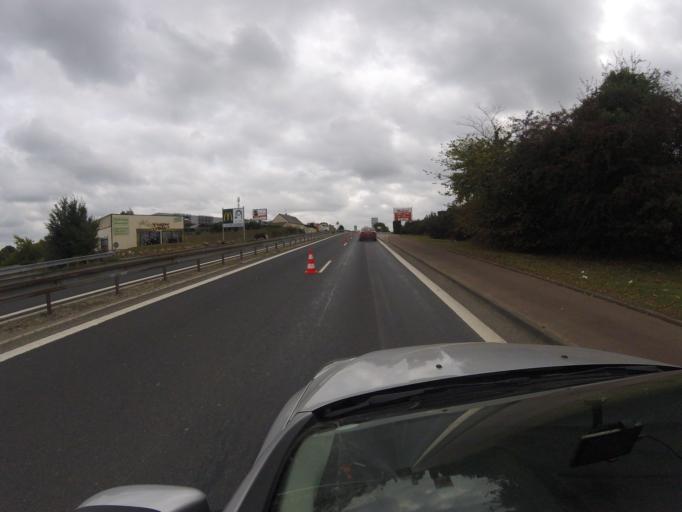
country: FR
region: Lower Normandy
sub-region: Departement de la Manche
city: La Glacerie
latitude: 49.6039
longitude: -1.5986
